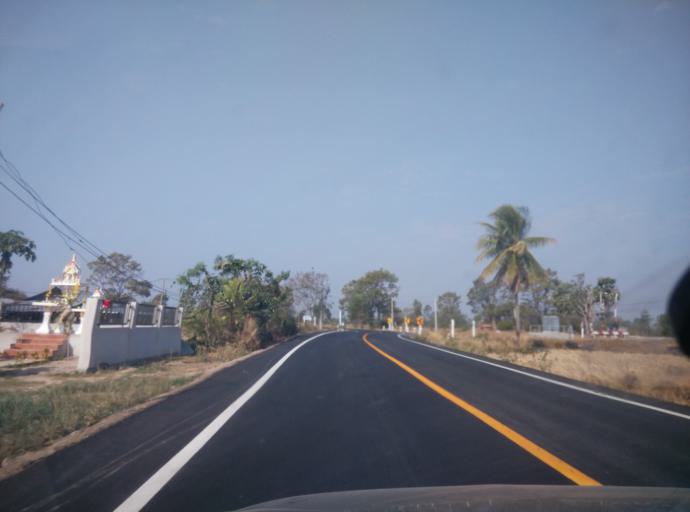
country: TH
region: Sisaket
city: Si Sa Ket
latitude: 15.1239
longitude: 104.2472
